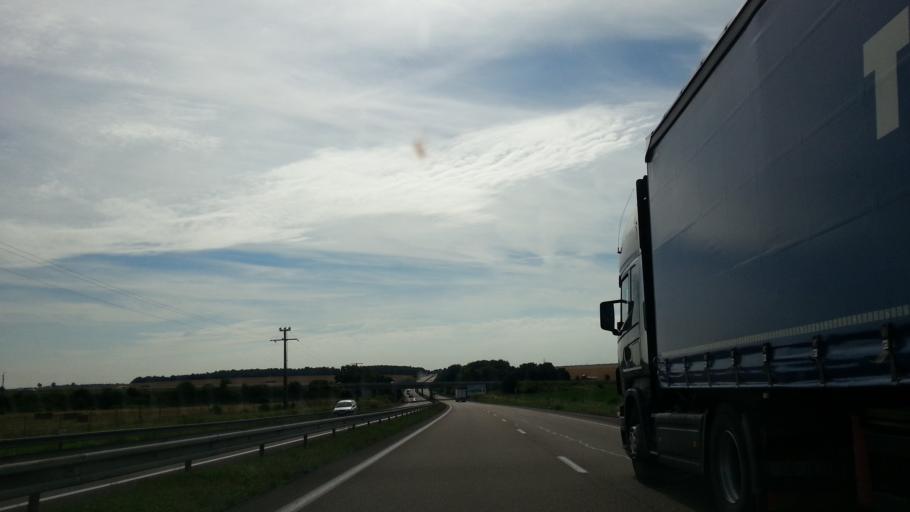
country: FR
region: Champagne-Ardenne
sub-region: Departement de la Marne
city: Fagnieres
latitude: 49.0481
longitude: 4.3019
